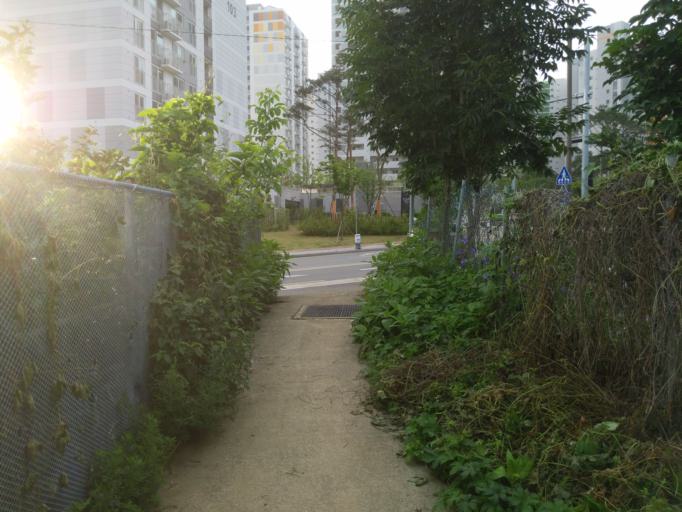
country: KR
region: Daegu
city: Hwawon
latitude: 35.8019
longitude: 128.5281
